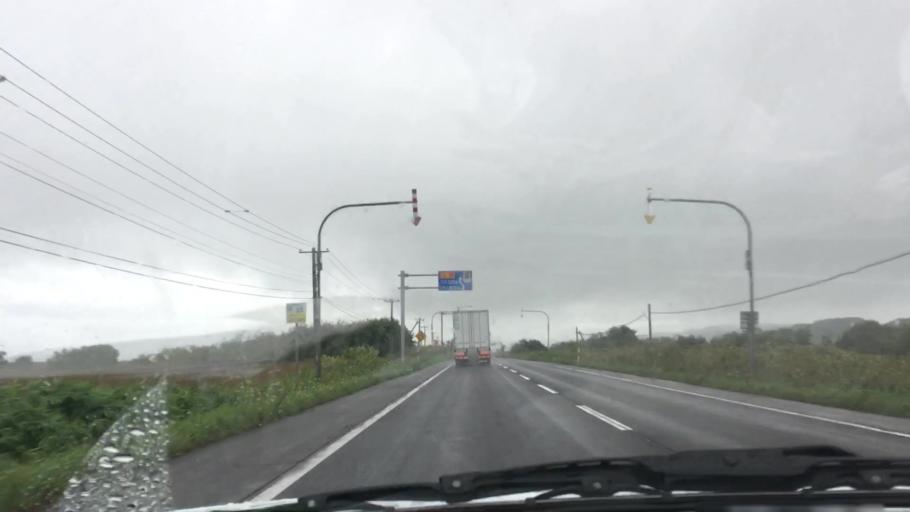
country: JP
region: Hokkaido
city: Niseko Town
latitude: 42.4233
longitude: 140.3143
